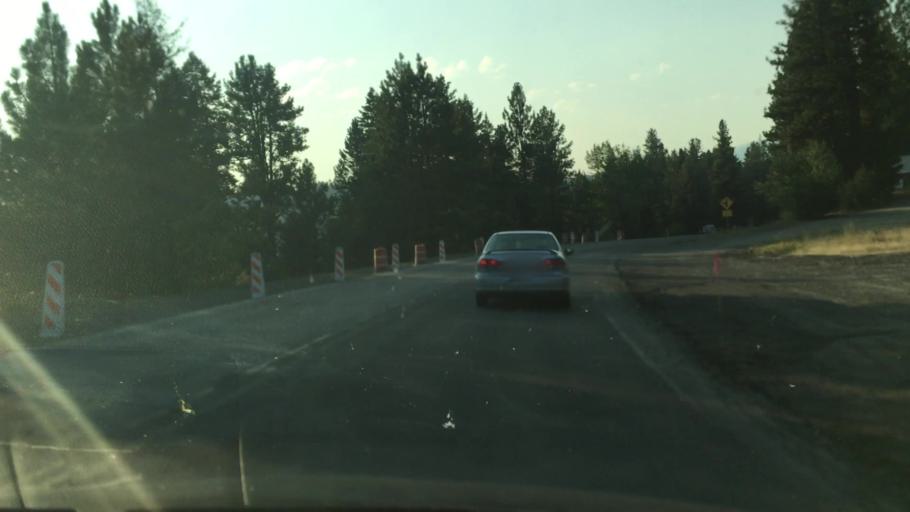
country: US
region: Idaho
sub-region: Valley County
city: McCall
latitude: 44.9314
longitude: -116.1644
